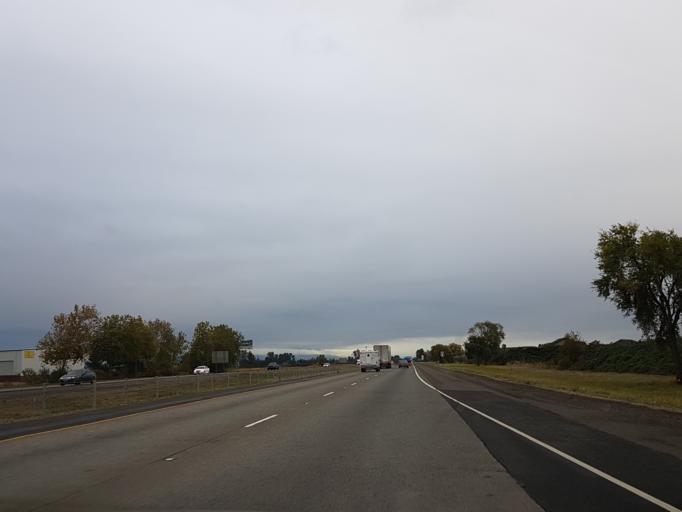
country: US
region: Oregon
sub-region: Linn County
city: Albany
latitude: 44.6244
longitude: -123.0623
